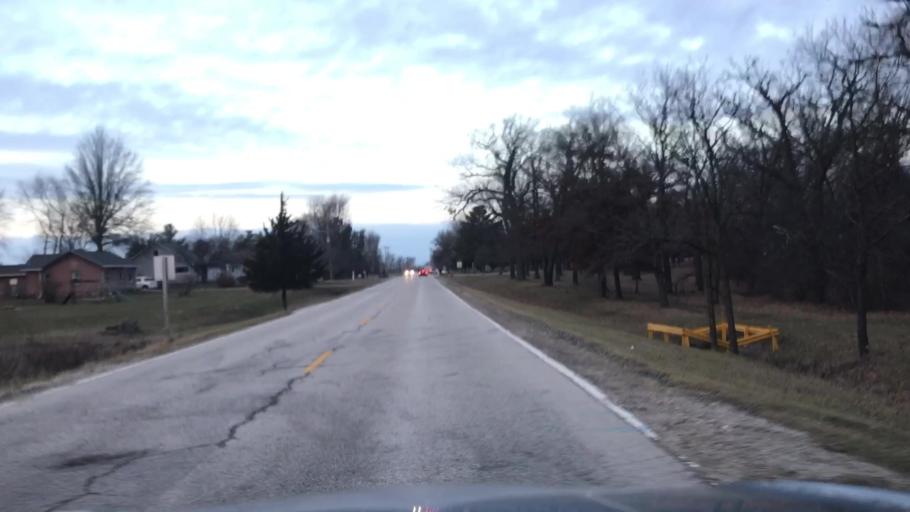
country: US
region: Illinois
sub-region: McLean County
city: Hudson
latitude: 40.6529
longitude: -88.9369
